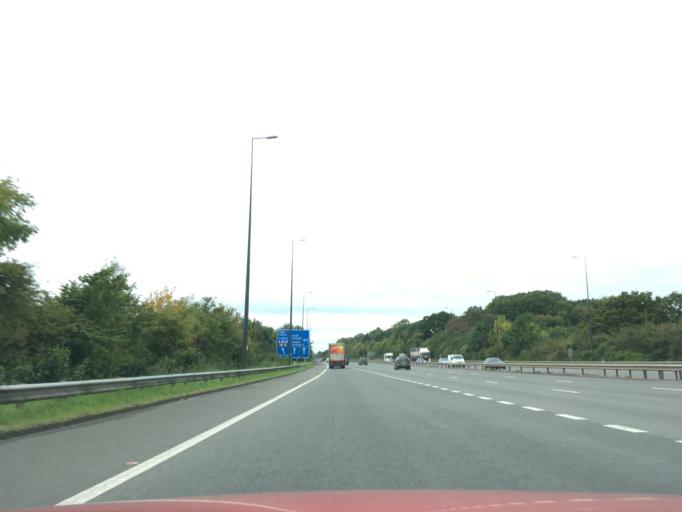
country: GB
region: Wales
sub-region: Monmouthshire
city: Magor
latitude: 51.5873
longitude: -2.8133
